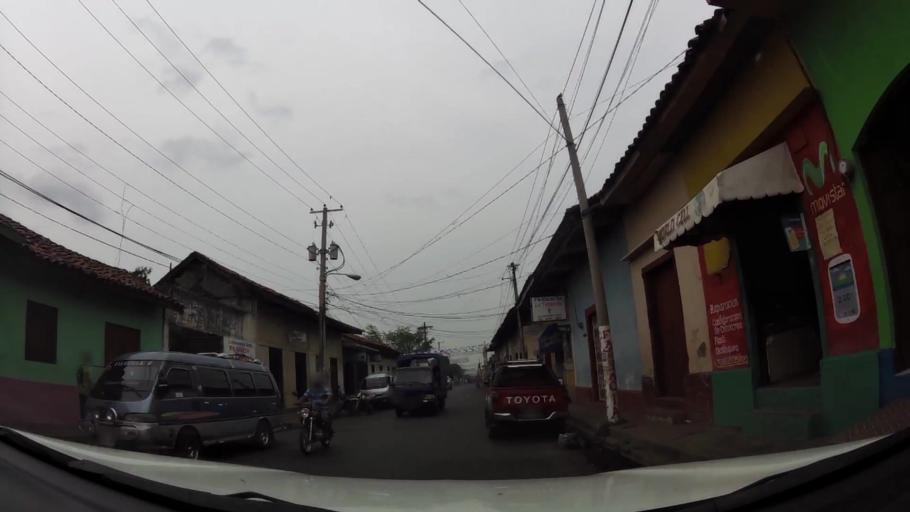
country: NI
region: Leon
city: Leon
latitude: 12.4425
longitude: -86.8724
